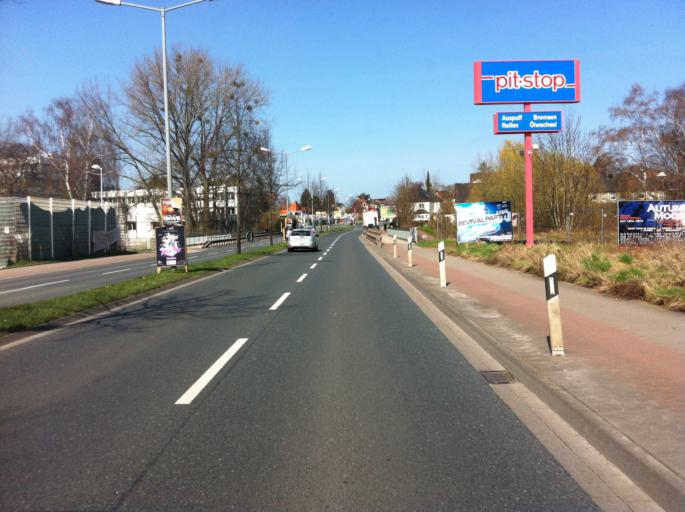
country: DE
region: North Rhine-Westphalia
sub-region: Regierungsbezirk Detmold
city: Minden
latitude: 52.2836
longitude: 8.9017
